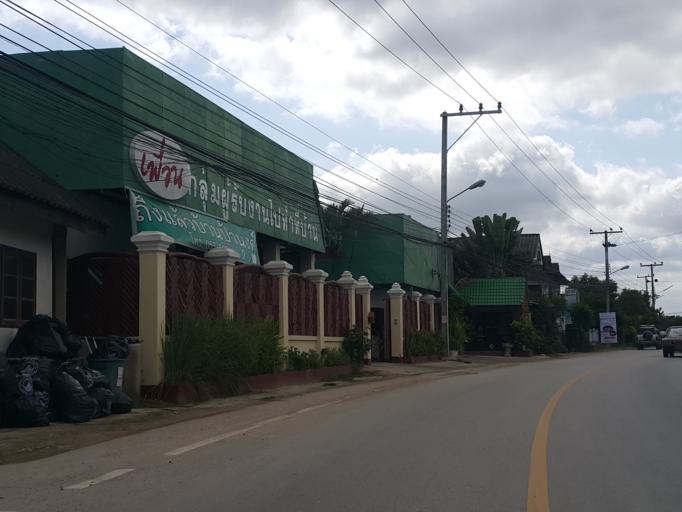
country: TH
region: Lamphun
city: Ban Thi
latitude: 18.6296
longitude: 99.1027
